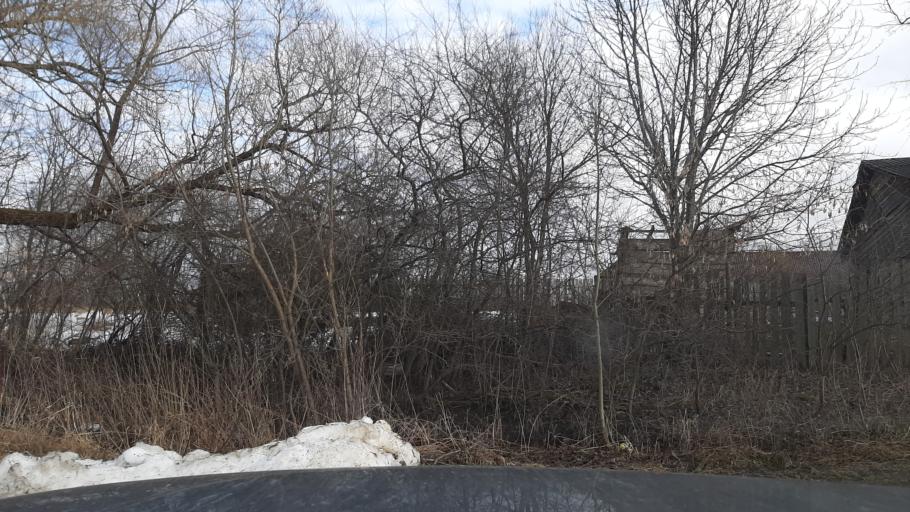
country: RU
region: Ivanovo
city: Teykovo
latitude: 56.8995
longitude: 40.6773
